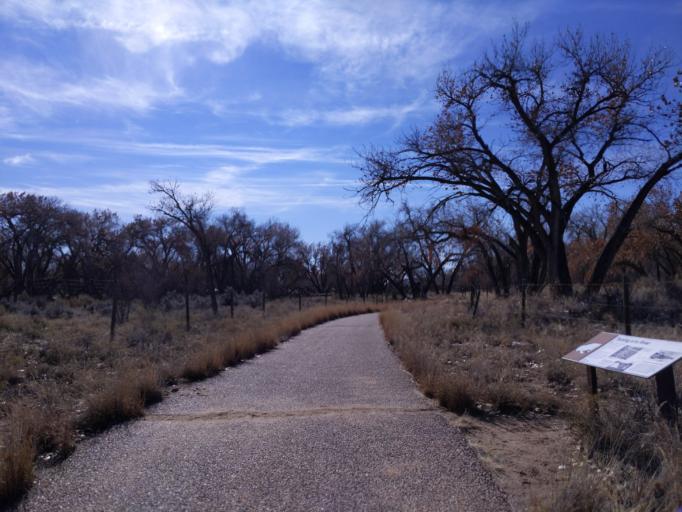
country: US
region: New Mexico
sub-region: Bernalillo County
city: Lee Acres
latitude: 35.1328
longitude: -106.6845
